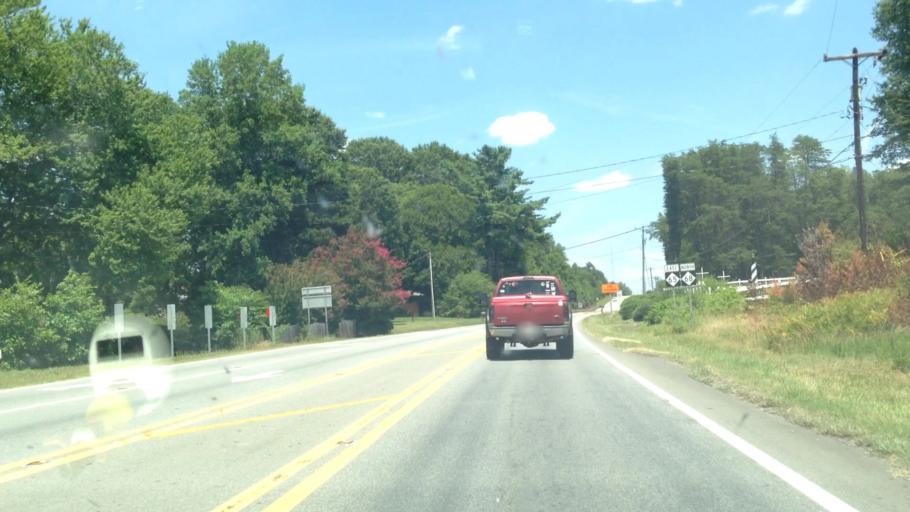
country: US
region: North Carolina
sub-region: Guilford County
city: Stokesdale
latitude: 36.2459
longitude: -79.9725
